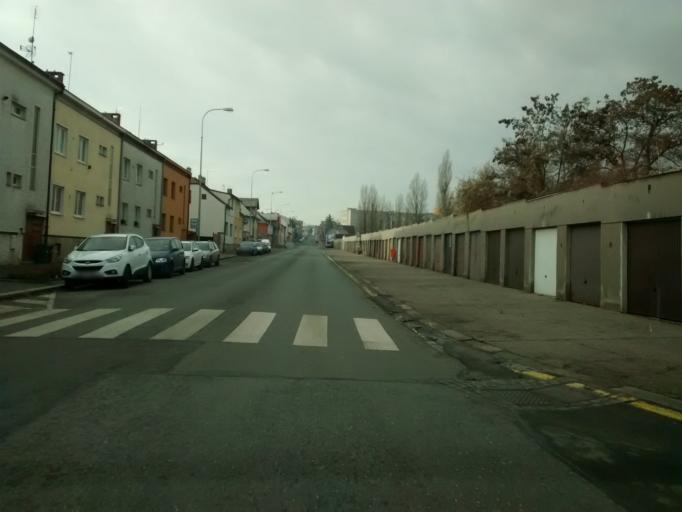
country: CZ
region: Central Bohemia
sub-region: Okres Mlada Boleslav
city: Mlada Boleslav
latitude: 50.4149
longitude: 14.9224
